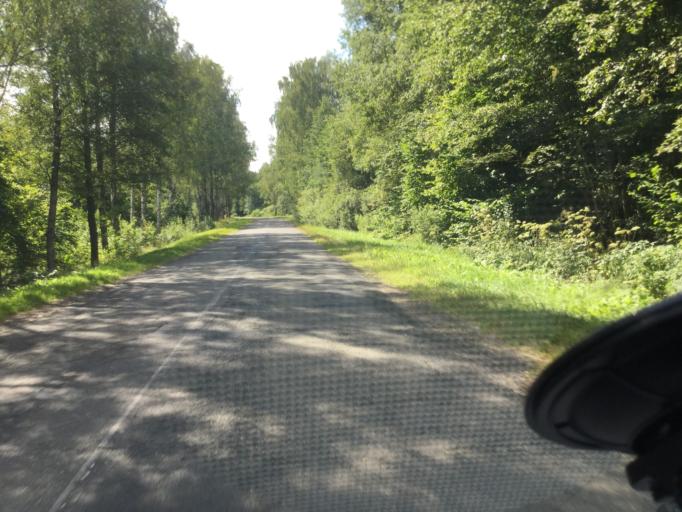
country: BY
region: Vitebsk
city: Chashniki
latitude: 55.2984
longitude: 29.3762
